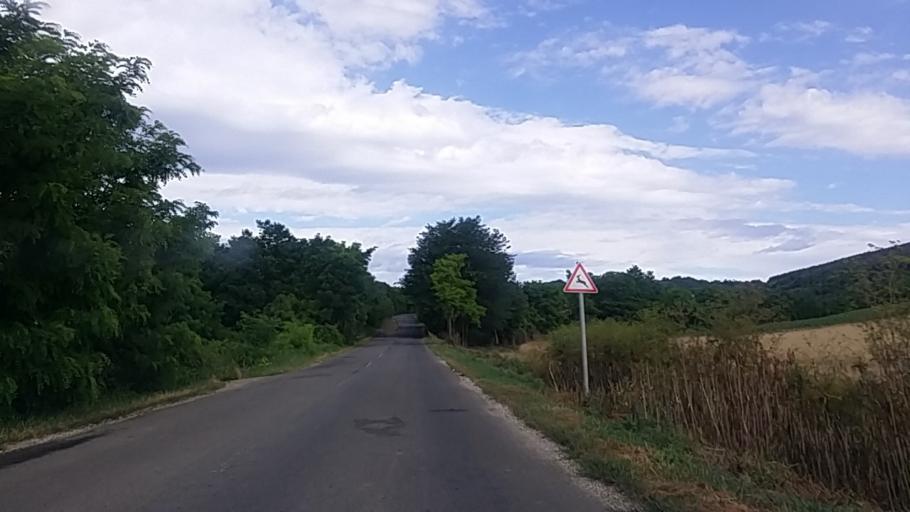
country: HU
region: Pest
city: Kosd
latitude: 47.8128
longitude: 19.2417
